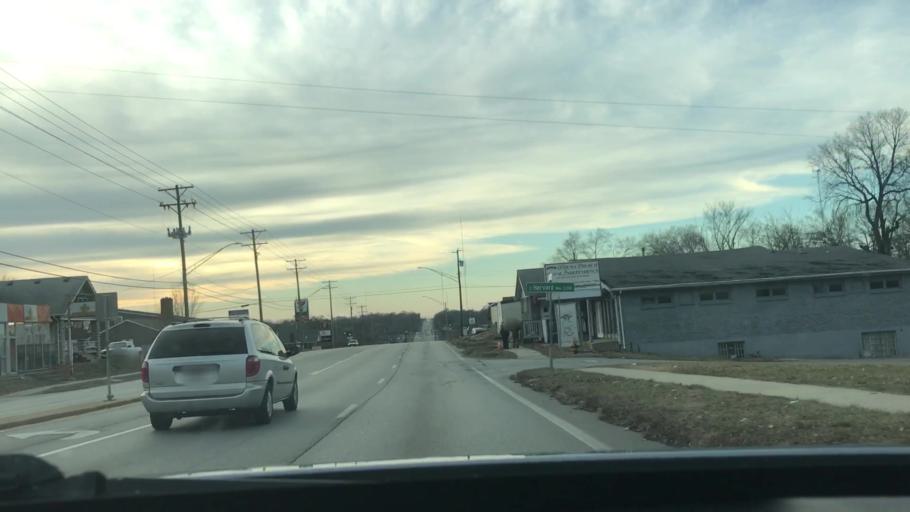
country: US
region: Missouri
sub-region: Jackson County
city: Sugar Creek
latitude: 39.0805
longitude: -94.4474
